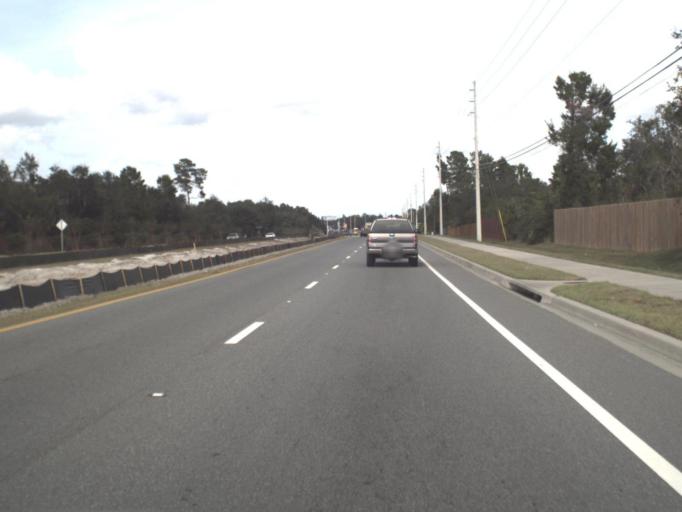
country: US
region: Florida
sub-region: Osceola County
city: Saint Cloud
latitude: 28.2917
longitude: -81.2430
